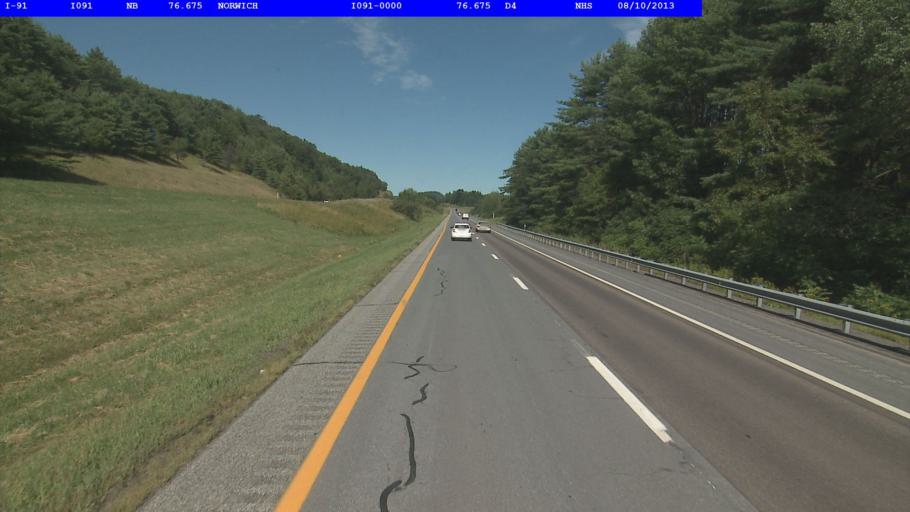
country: US
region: New Hampshire
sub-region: Grafton County
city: Hanover
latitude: 43.7271
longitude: -72.2845
